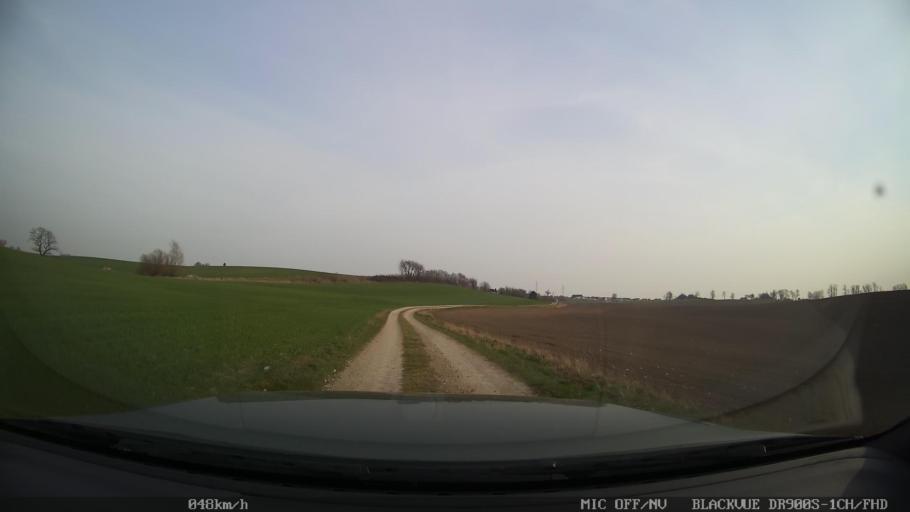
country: SE
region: Skane
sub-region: Ystads Kommun
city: Ystad
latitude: 55.4553
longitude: 13.7918
